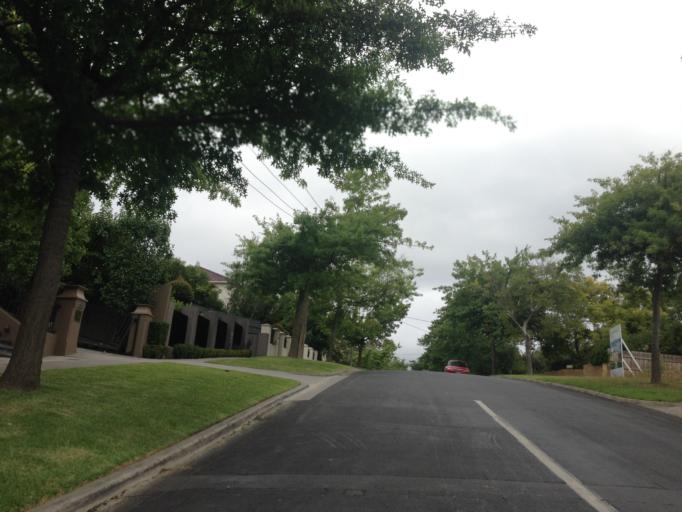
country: AU
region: Victoria
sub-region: Boroondara
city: Balwyn North
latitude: -37.7955
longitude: 145.0923
